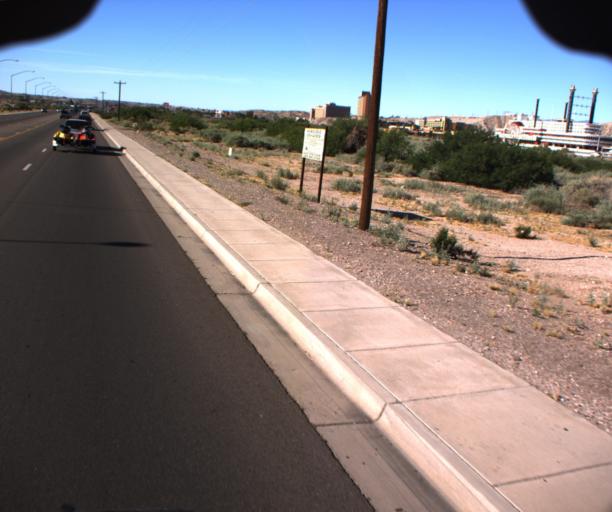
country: US
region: Nevada
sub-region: Clark County
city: Laughlin
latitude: 35.1624
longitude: -114.5666
